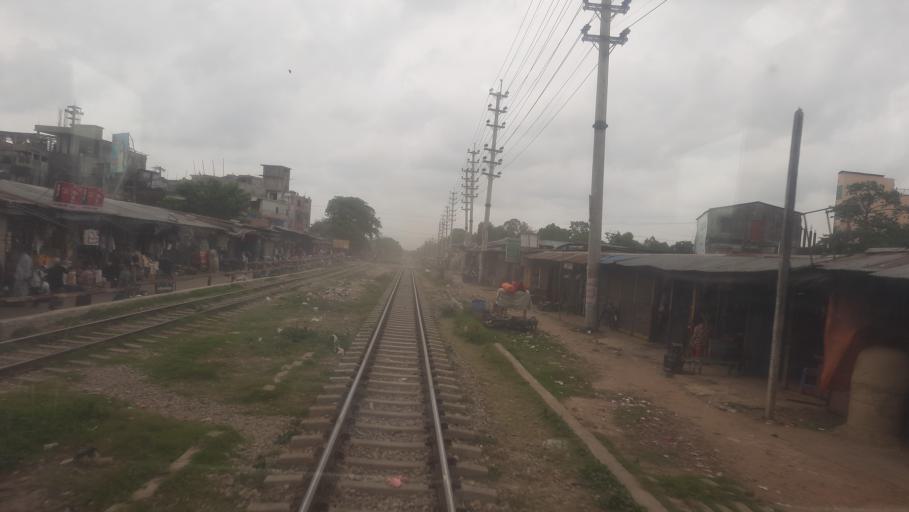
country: BD
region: Chittagong
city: Chhagalnaiya
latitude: 22.8940
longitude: 91.5361
